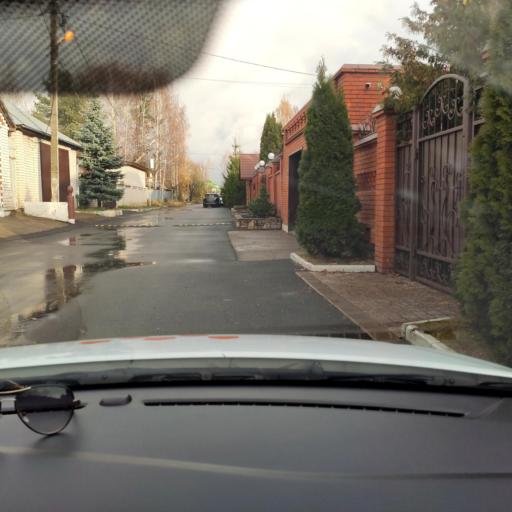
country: RU
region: Tatarstan
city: Stolbishchi
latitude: 55.7450
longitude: 49.2423
